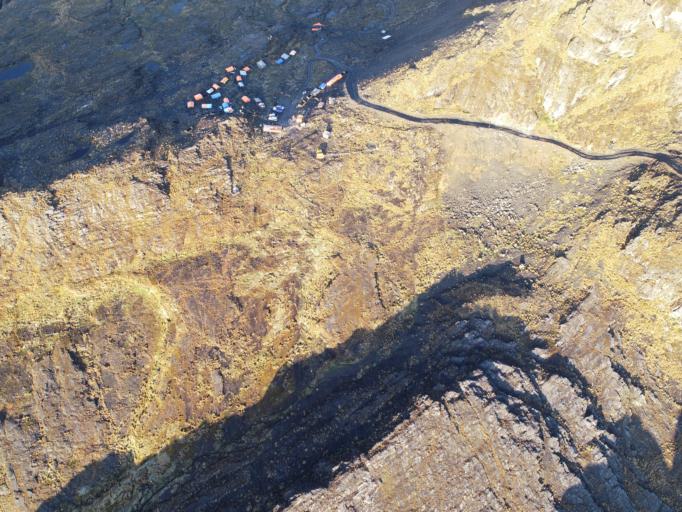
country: PE
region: Puno
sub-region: San Antonio De Putina
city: Sina
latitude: -14.7387
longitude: -69.0474
